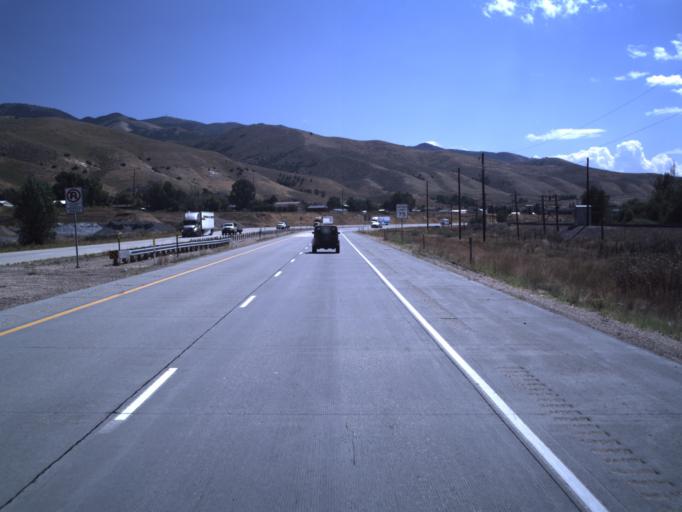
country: US
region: Utah
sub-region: Morgan County
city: Mountain Green
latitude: 41.1112
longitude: -111.7555
